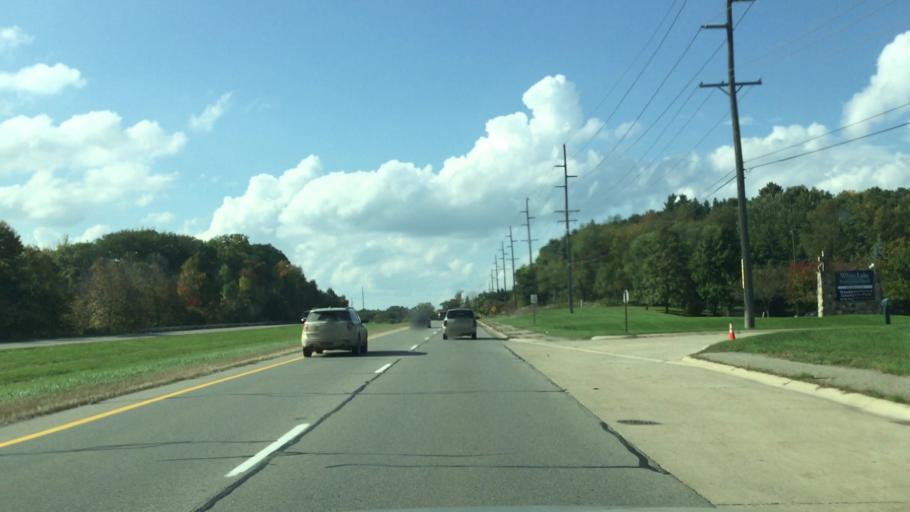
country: US
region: Michigan
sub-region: Oakland County
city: Milford
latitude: 42.6516
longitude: -83.5459
